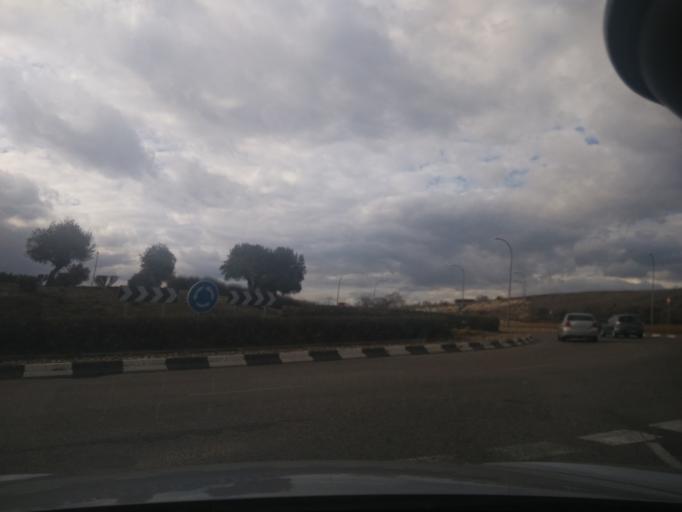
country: ES
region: Madrid
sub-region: Provincia de Madrid
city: Alcobendas
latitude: 40.5487
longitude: -3.6623
